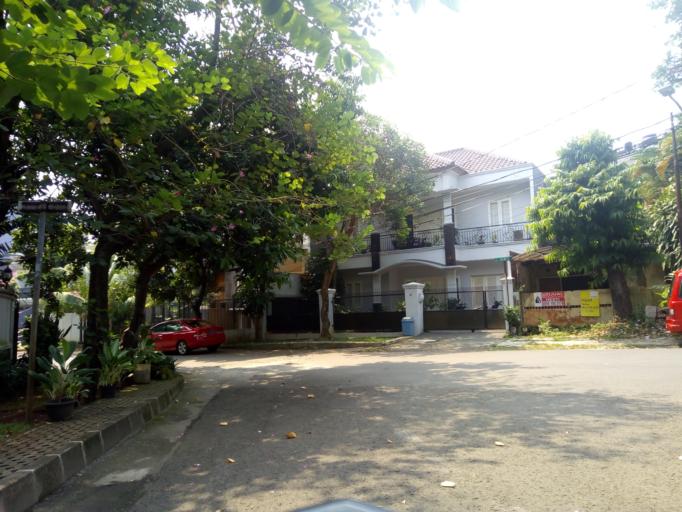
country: ID
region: Jakarta Raya
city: Jakarta
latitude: -6.2370
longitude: 106.7914
